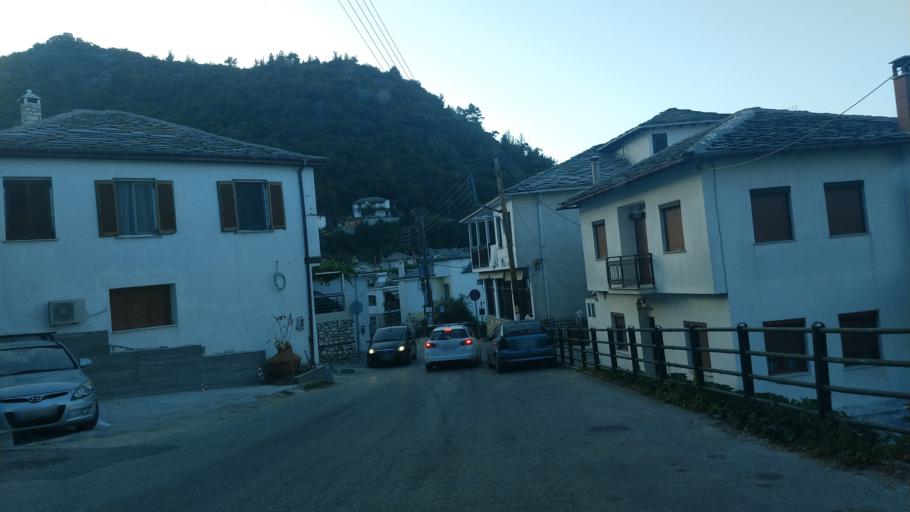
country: GR
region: East Macedonia and Thrace
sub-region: Nomos Kavalas
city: Potamia
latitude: 40.7305
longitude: 24.7298
